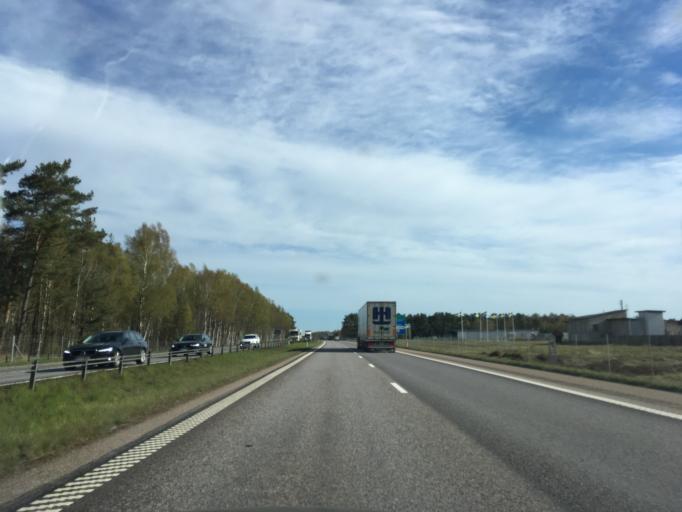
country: SE
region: Halland
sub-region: Laholms Kommun
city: Mellbystrand
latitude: 56.4931
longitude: 12.9549
